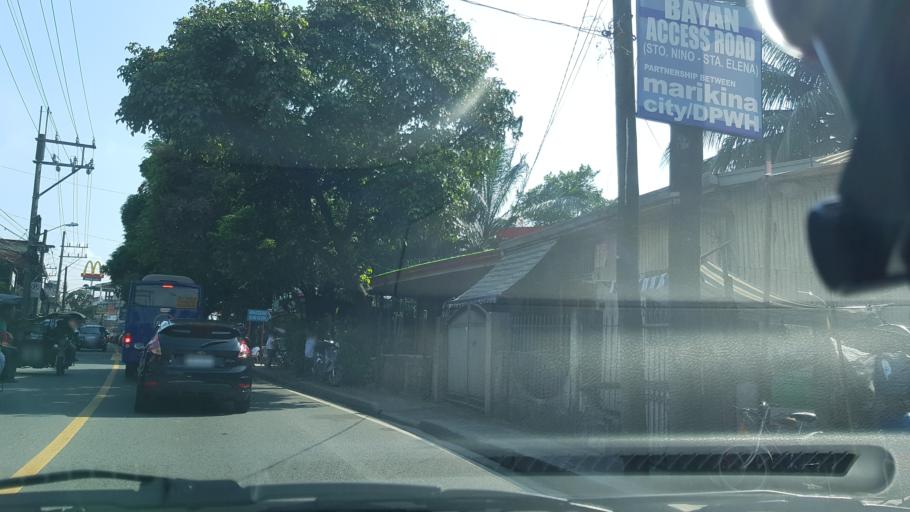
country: PH
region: Metro Manila
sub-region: Marikina
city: Calumpang
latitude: 14.6387
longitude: 121.0941
